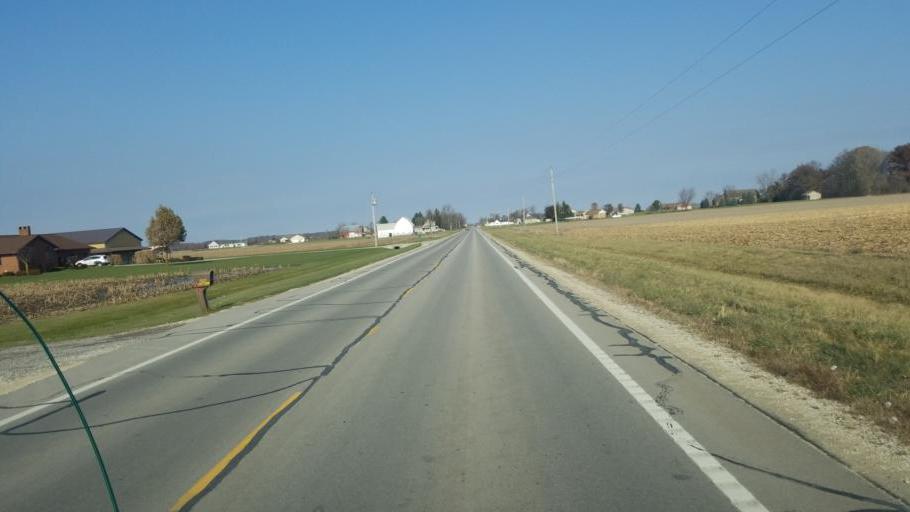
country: US
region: Ohio
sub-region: Mercer County
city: Coldwater
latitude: 40.5185
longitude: -84.6286
